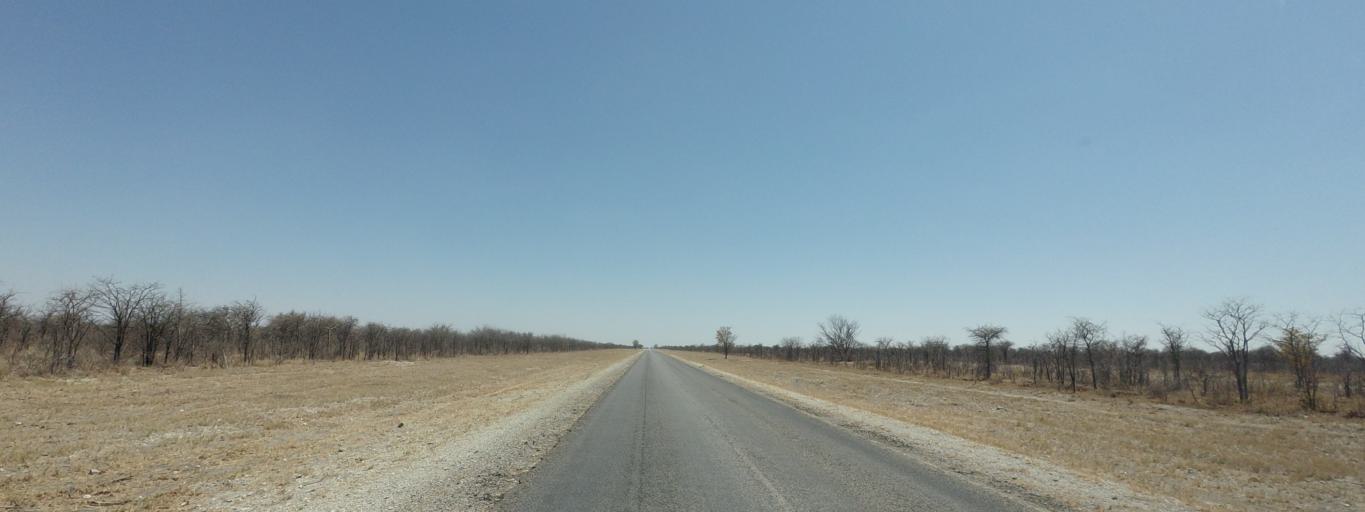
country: BW
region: Central
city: Nata
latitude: -20.3440
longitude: 26.3149
